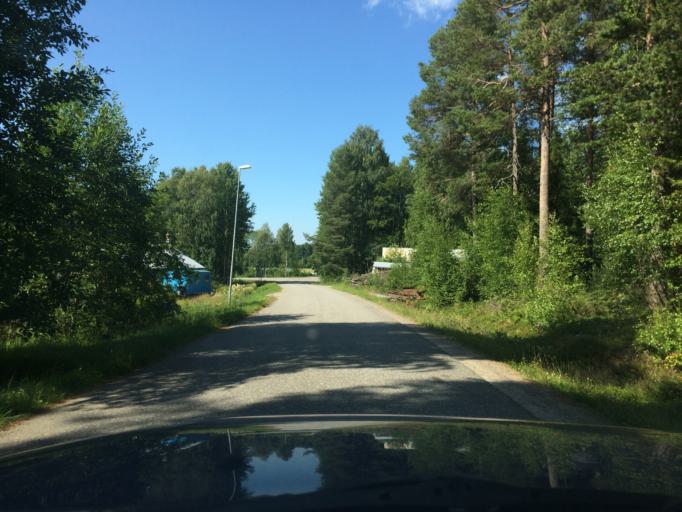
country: SE
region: Norrbotten
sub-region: Pitea Kommun
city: Norrfjarden
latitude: 65.3655
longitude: 21.4133
